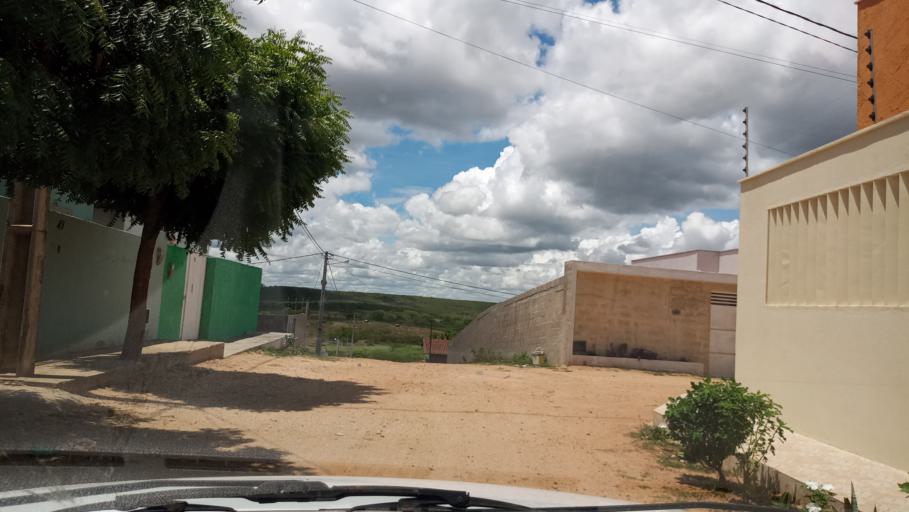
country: BR
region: Rio Grande do Norte
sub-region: Sao Paulo Do Potengi
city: Sao Paulo do Potengi
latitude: -5.8998
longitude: -35.7714
